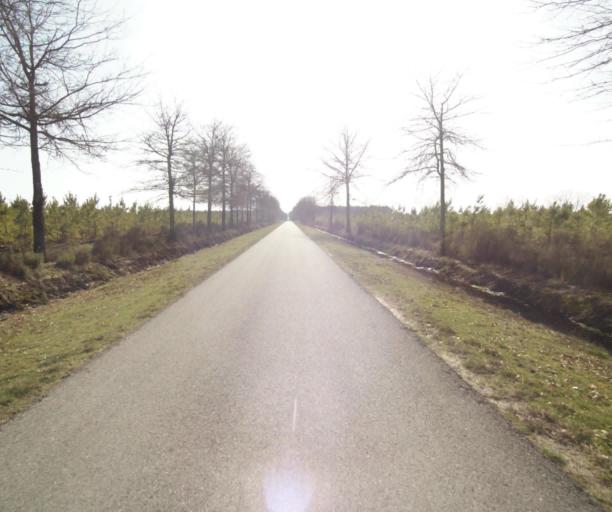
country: FR
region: Aquitaine
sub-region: Departement des Landes
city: Roquefort
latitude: 44.1676
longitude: -0.1638
